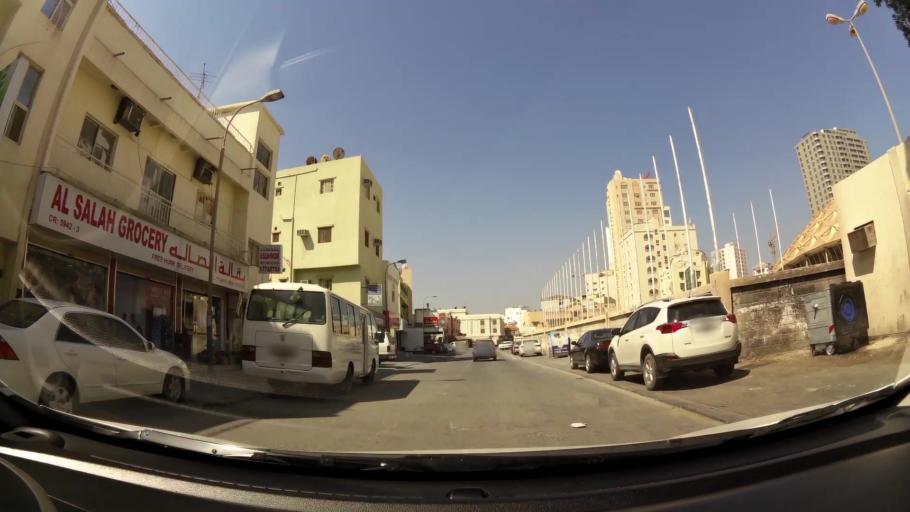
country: BH
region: Manama
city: Manama
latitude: 26.2122
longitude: 50.6013
